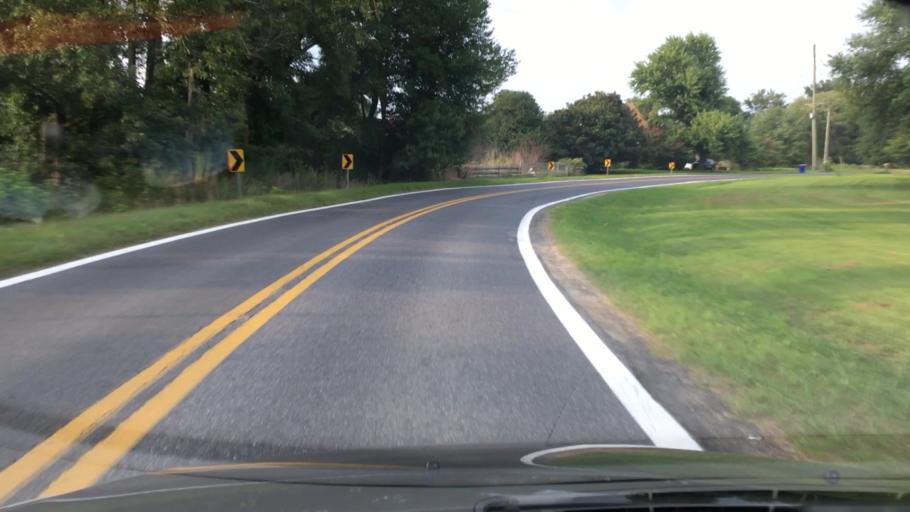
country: US
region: Delaware
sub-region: Sussex County
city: Ocean View
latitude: 38.5018
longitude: -75.1312
